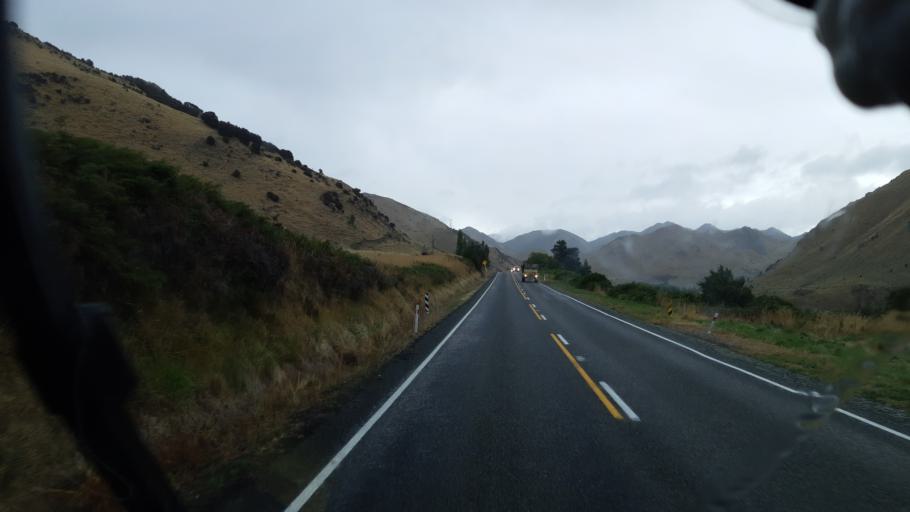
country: NZ
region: Canterbury
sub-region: Hurunui District
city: Amberley
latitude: -42.6724
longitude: 172.7758
